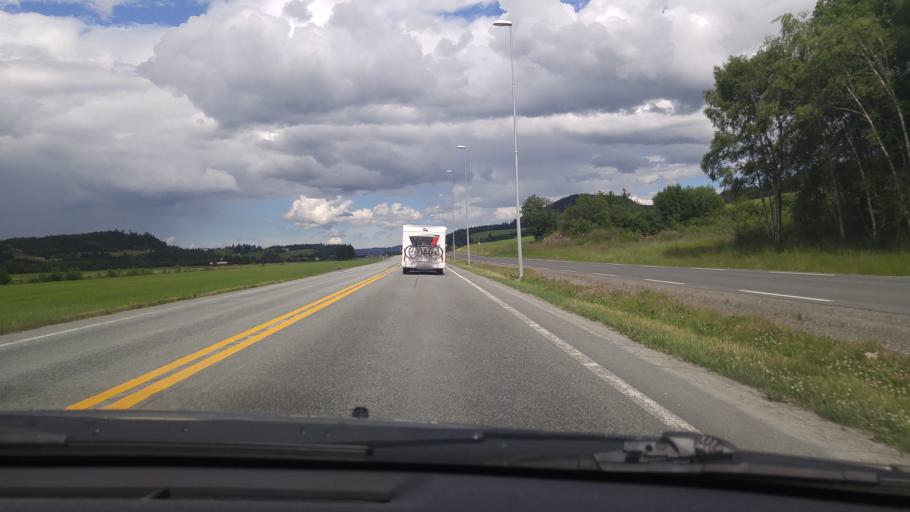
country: NO
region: Nord-Trondelag
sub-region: Steinkjer
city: Steinkjer
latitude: 63.9405
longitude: 11.4207
